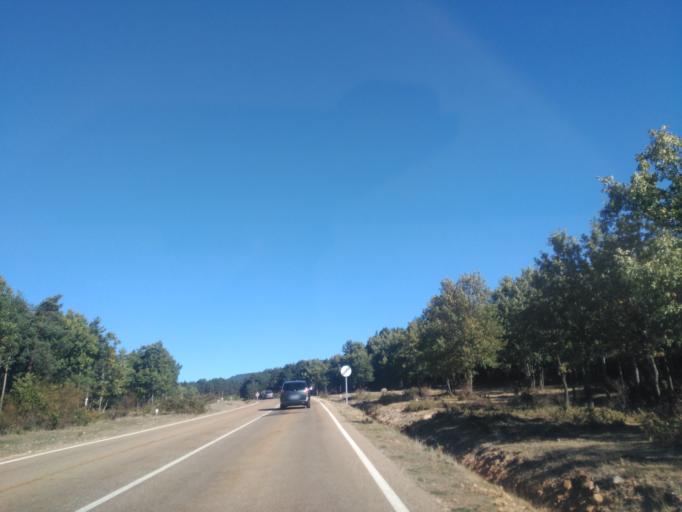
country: ES
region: Castille and Leon
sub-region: Provincia de Soria
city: Vinuesa
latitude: 41.9461
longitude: -2.7732
